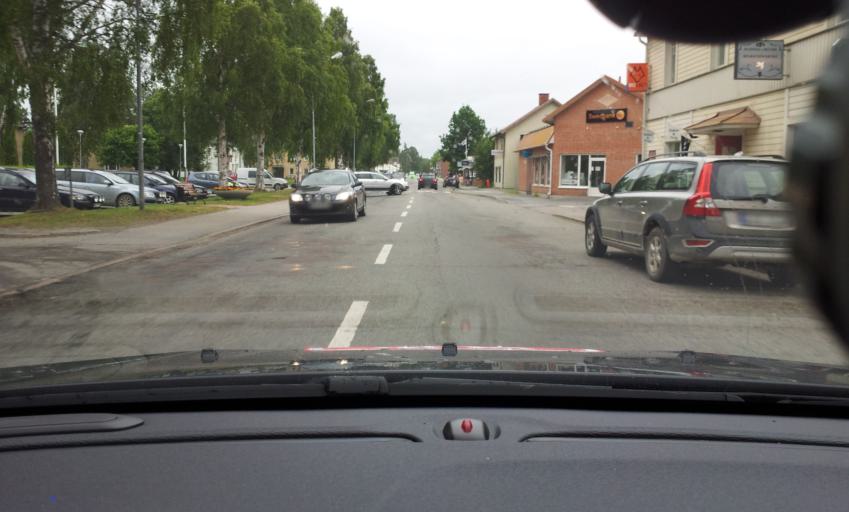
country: SE
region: Jaemtland
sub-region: Ragunda Kommun
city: Hammarstrand
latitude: 63.1101
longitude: 16.3541
